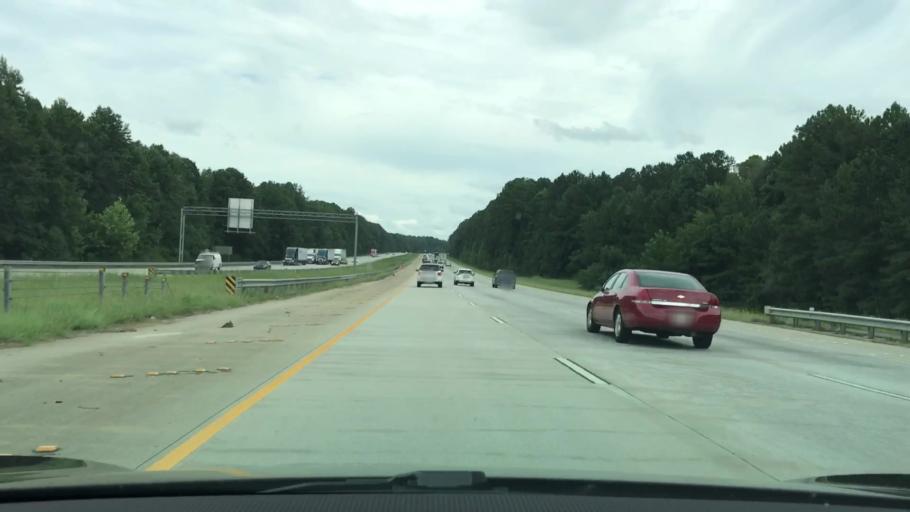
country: US
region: Georgia
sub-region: Coweta County
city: Grantville
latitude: 33.2561
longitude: -84.8056
